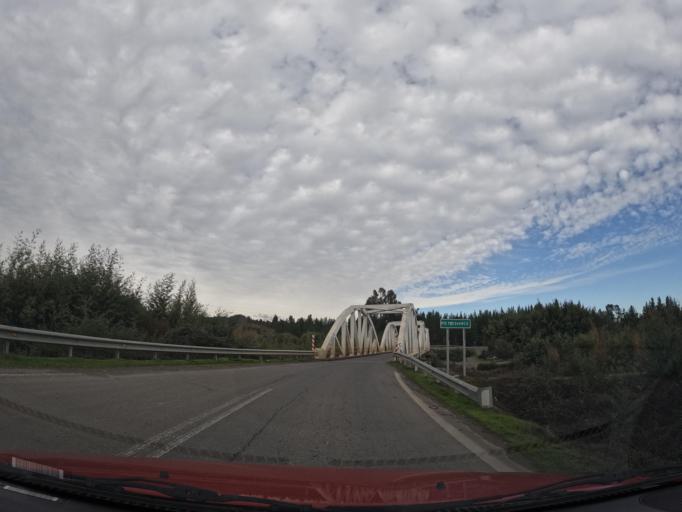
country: CL
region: Maule
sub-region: Provincia de Linares
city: Linares
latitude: -35.9082
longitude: -71.4915
